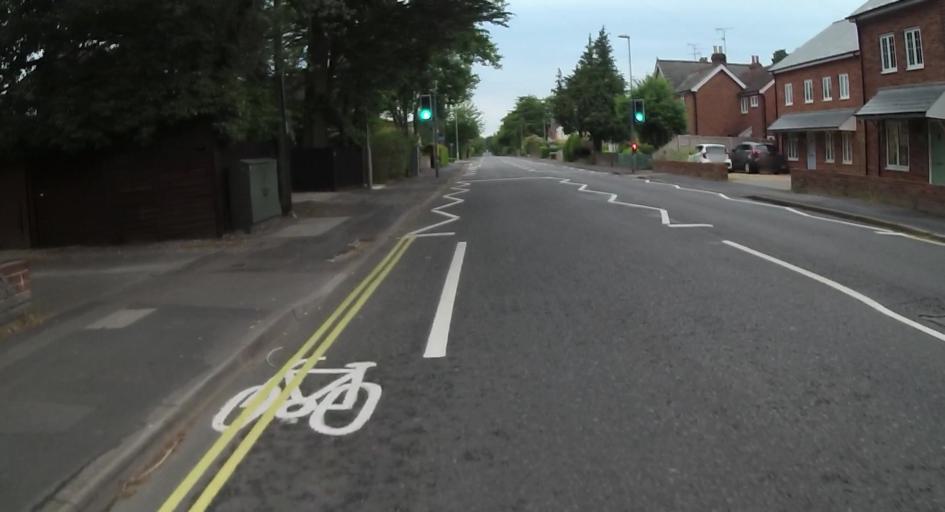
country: GB
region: England
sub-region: Hampshire
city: Fleet
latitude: 51.2793
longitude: -0.8262
